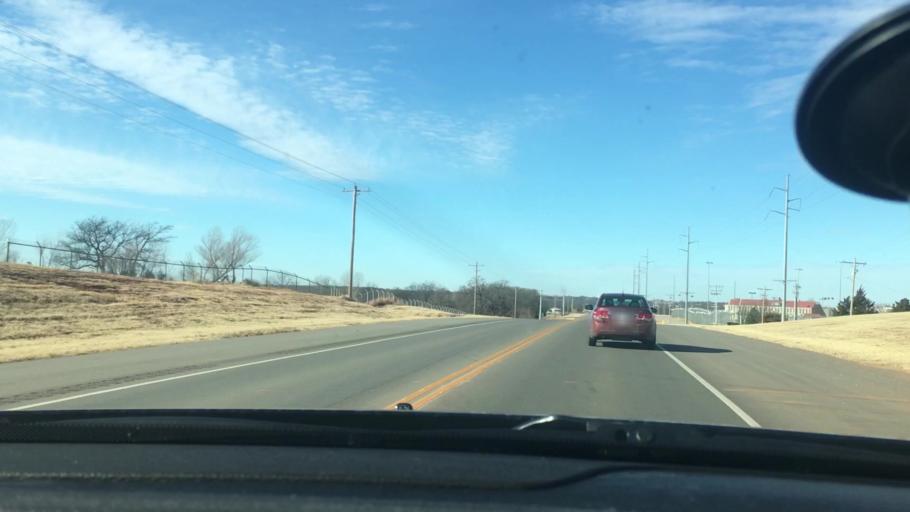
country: US
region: Oklahoma
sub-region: Cleveland County
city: Lexington
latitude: 35.0150
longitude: -97.2163
